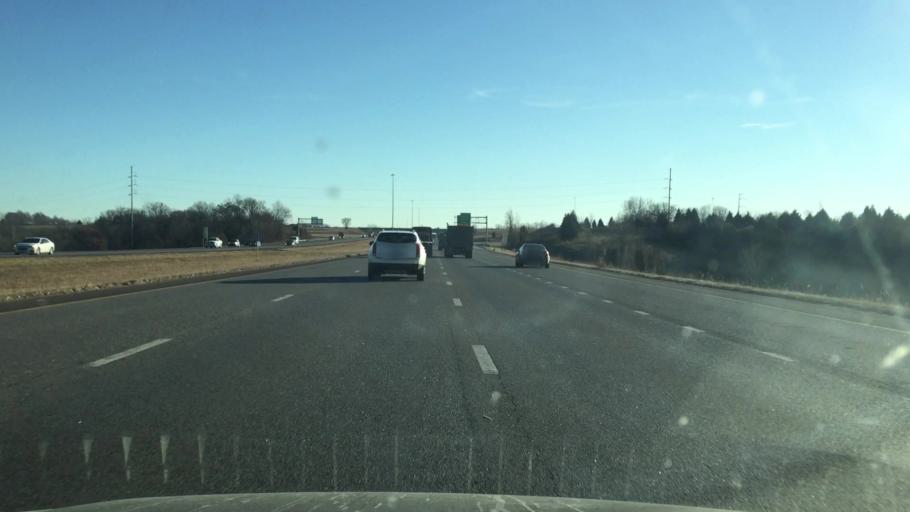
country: US
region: Kansas
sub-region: Wyandotte County
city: Edwardsville
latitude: 39.0195
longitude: -94.7856
